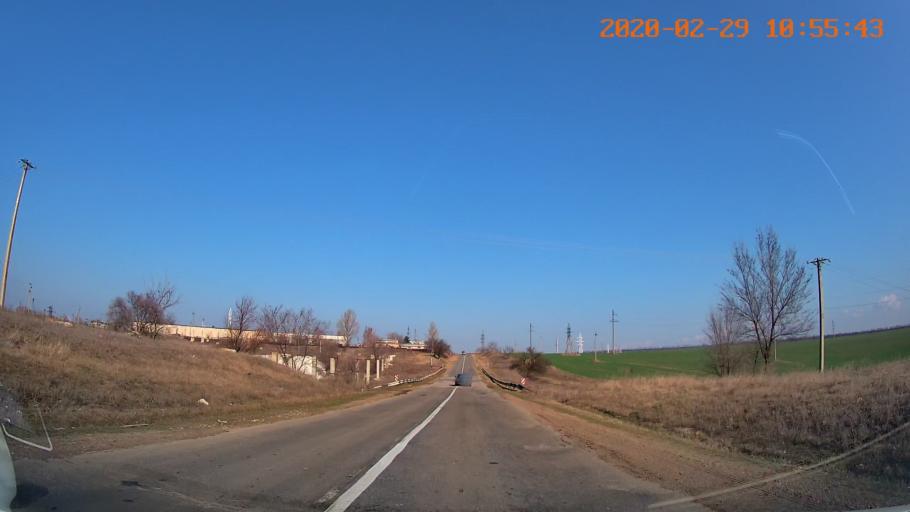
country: MD
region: Telenesti
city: Grigoriopol
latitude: 47.1370
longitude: 29.3254
